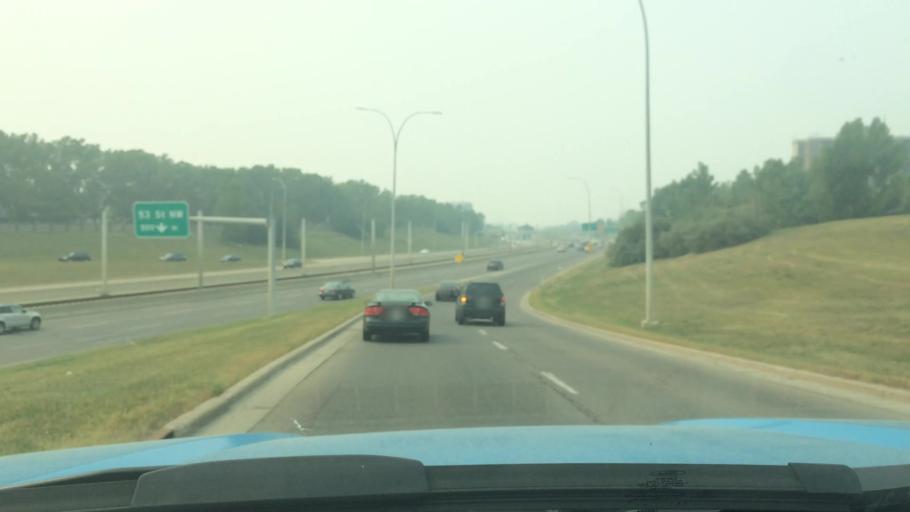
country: CA
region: Alberta
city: Calgary
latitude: 51.0993
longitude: -114.1506
